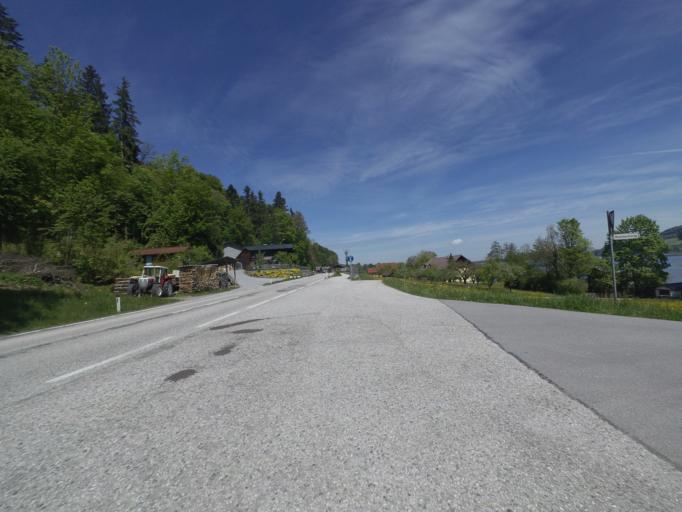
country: AT
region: Salzburg
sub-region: Politischer Bezirk Salzburg-Umgebung
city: Obertrum am See
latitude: 47.9457
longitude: 13.0690
